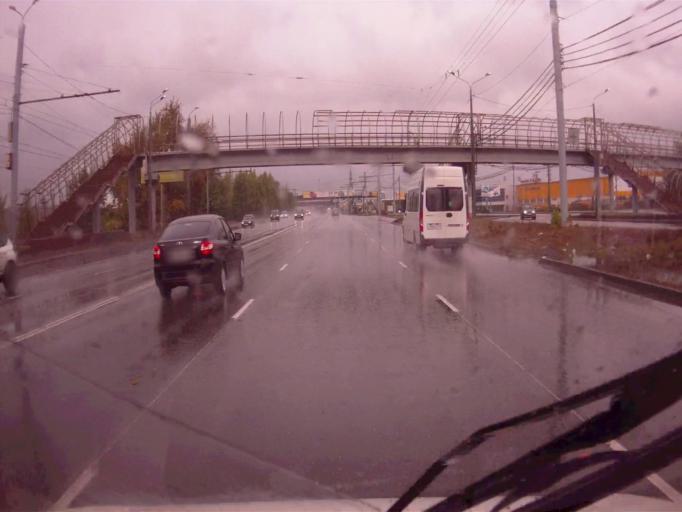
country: RU
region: Chelyabinsk
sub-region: Gorod Chelyabinsk
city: Chelyabinsk
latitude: 55.2006
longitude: 61.3858
